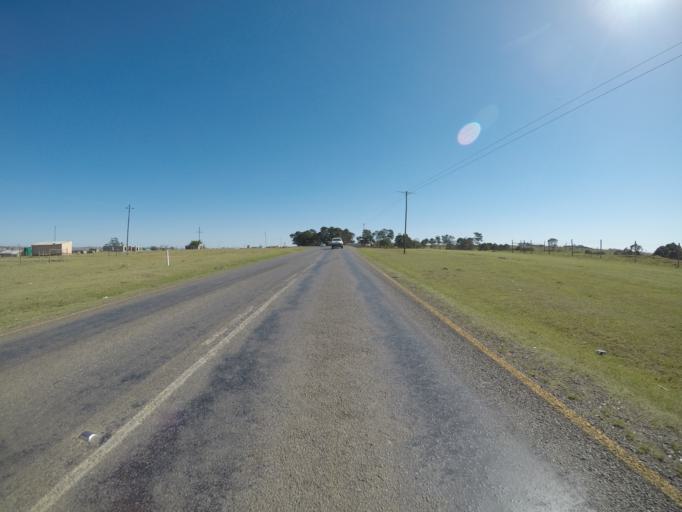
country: ZA
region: Eastern Cape
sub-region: OR Tambo District Municipality
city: Mthatha
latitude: -31.7925
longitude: 28.7452
